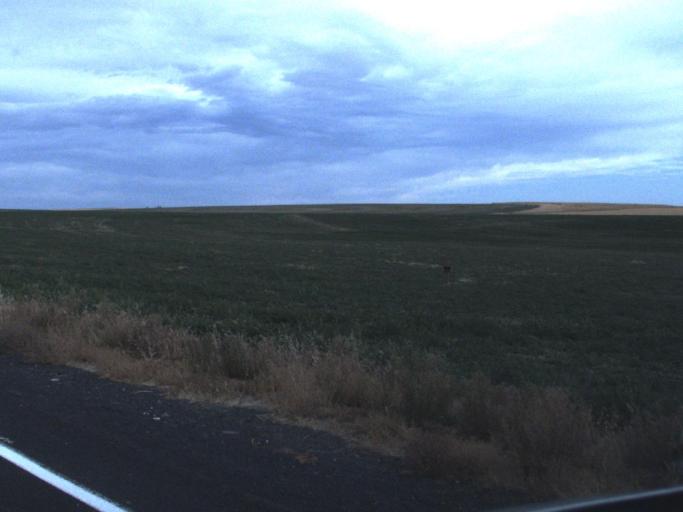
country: US
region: Washington
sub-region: Okanogan County
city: Coulee Dam
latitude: 47.5773
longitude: -118.7859
